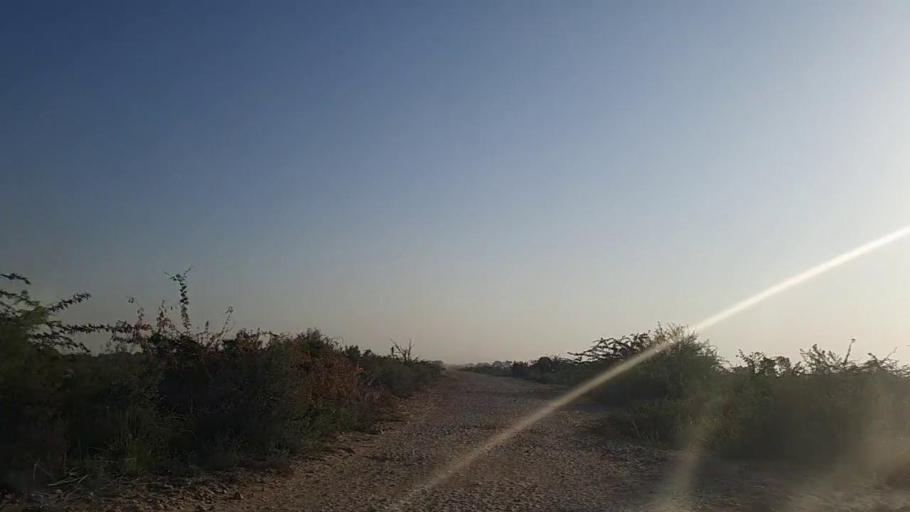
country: PK
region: Sindh
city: Jati
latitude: 24.4380
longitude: 68.1928
